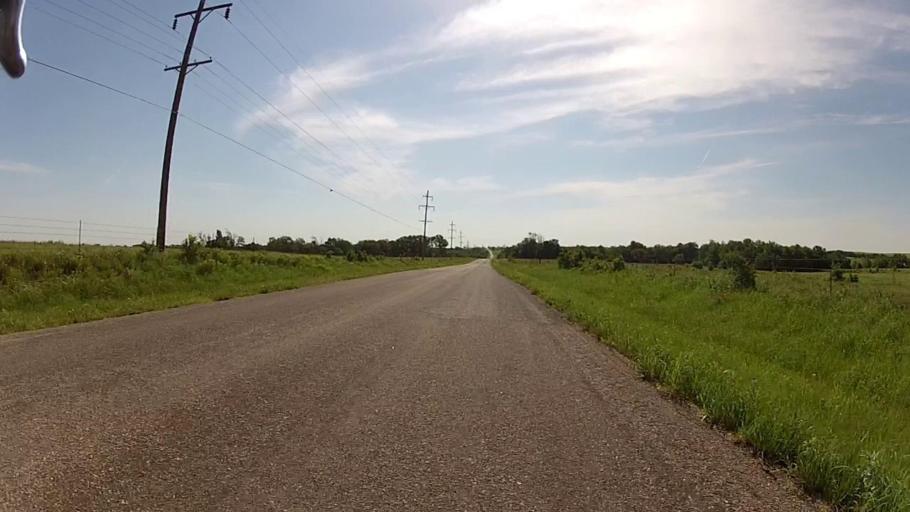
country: US
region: Kansas
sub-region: Cowley County
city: Winfield
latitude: 37.0710
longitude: -96.6714
